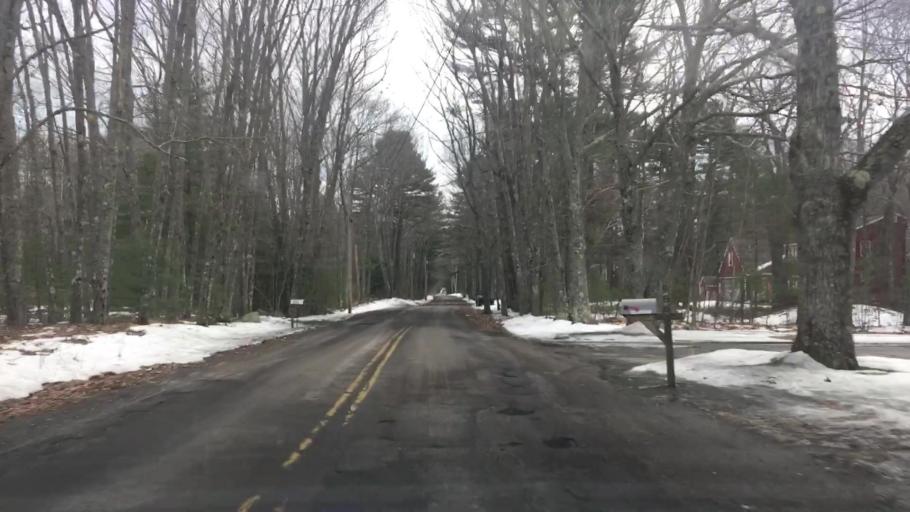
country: US
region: Maine
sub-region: York County
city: Wells Beach Station
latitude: 43.3430
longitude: -70.6145
